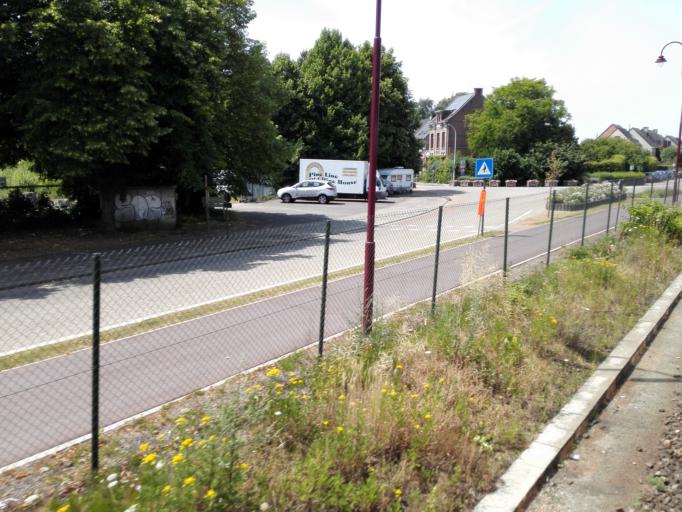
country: BE
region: Flanders
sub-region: Provincie Antwerpen
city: Boechout
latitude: 51.1657
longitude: 4.4900
